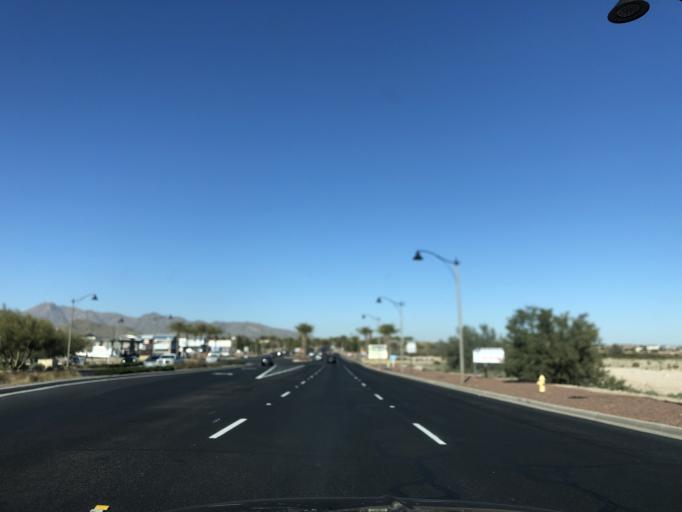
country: US
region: Arizona
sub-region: Maricopa County
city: Citrus Park
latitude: 33.4633
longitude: -112.5042
